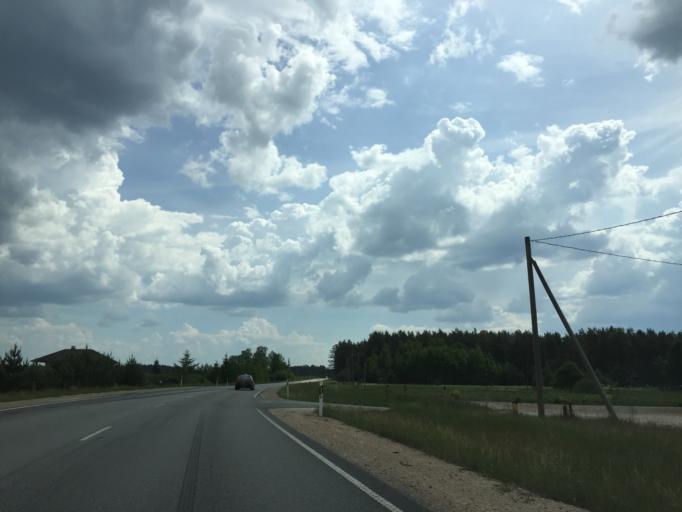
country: LV
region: Salaspils
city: Salaspils
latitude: 56.8984
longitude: 24.4277
